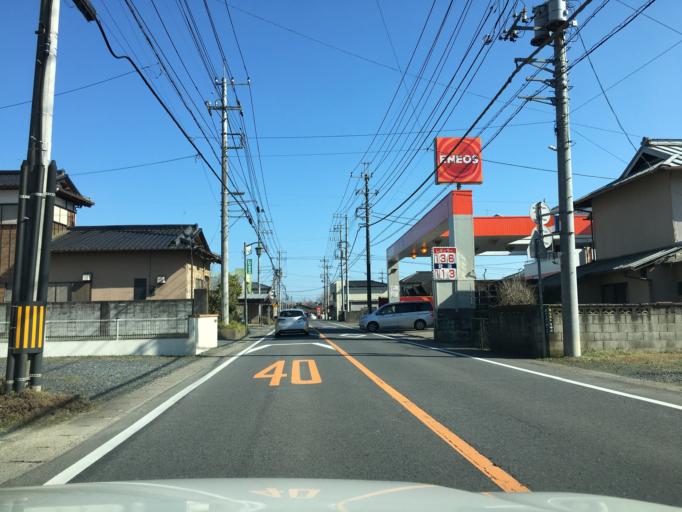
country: JP
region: Ibaraki
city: Omiya
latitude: 36.5509
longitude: 140.3269
